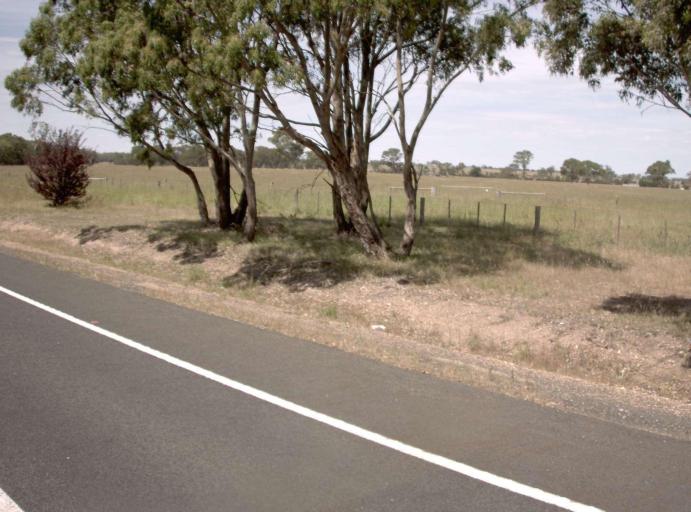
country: AU
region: Victoria
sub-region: Wellington
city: Sale
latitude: -37.9580
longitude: 147.0967
